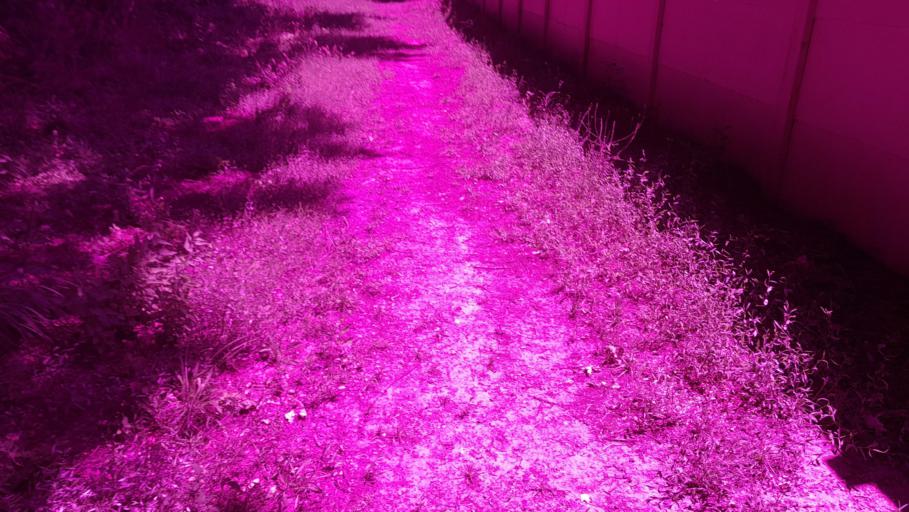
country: FR
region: Pays de la Loire
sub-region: Departement de la Loire-Atlantique
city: Oudon
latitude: 47.3515
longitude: -1.2841
